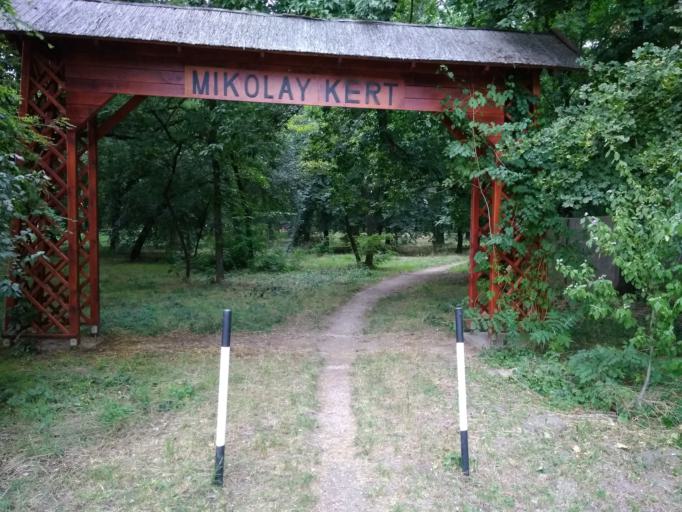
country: HU
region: Bekes
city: Oroshaza
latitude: 46.5675
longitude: 20.6638
